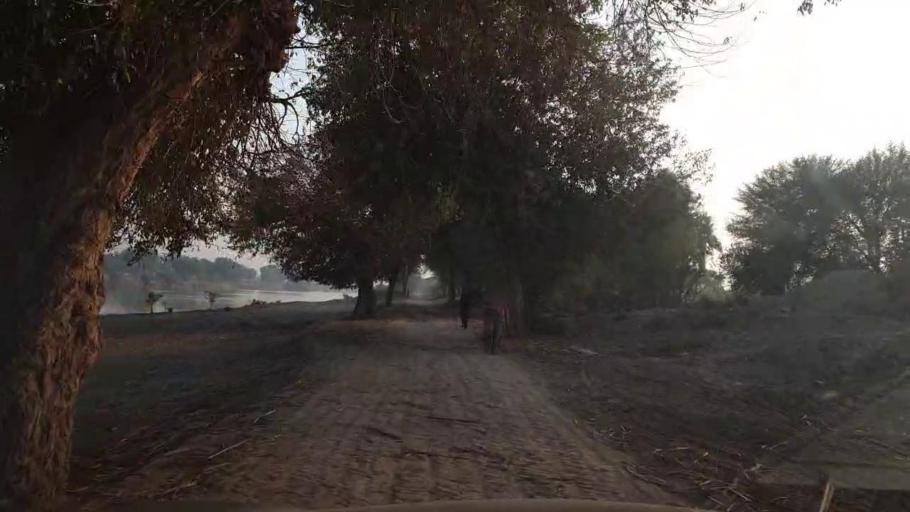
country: PK
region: Sindh
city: Ubauro
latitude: 28.3120
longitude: 69.7898
